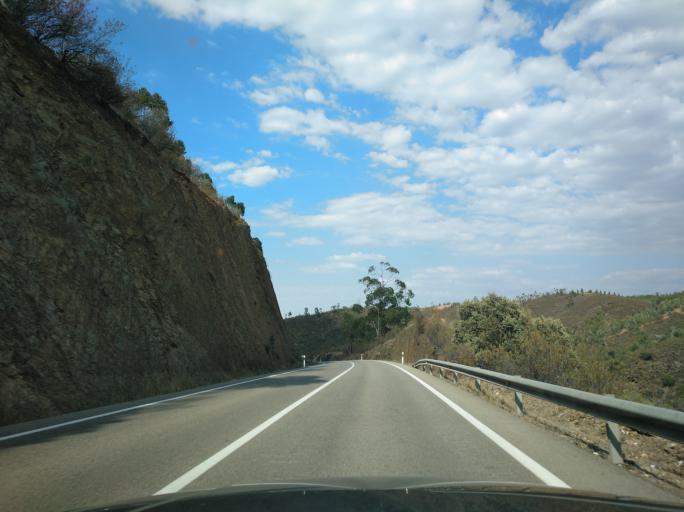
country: ES
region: Andalusia
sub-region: Provincia de Huelva
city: Santa Barbara de Casa
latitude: 37.8742
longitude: -7.2163
